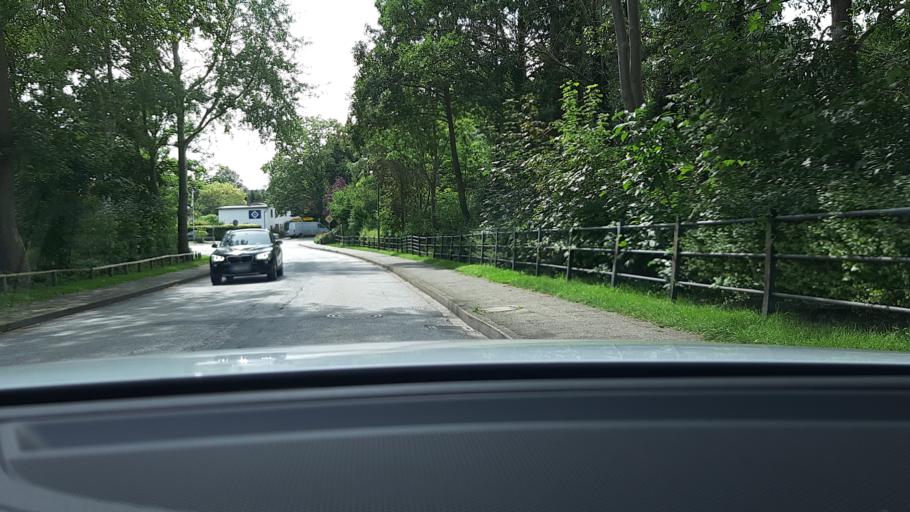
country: DE
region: Schleswig-Holstein
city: Reinfeld
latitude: 53.8321
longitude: 10.4781
